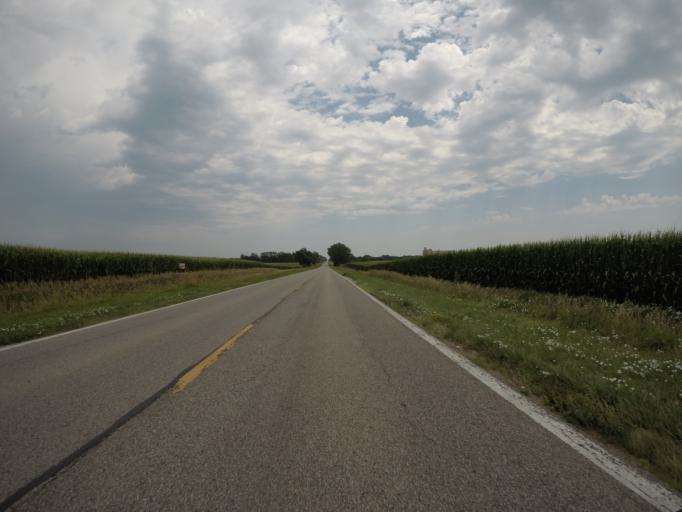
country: US
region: Nebraska
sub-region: Adams County
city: Hastings
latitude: 40.5970
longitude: -98.5226
